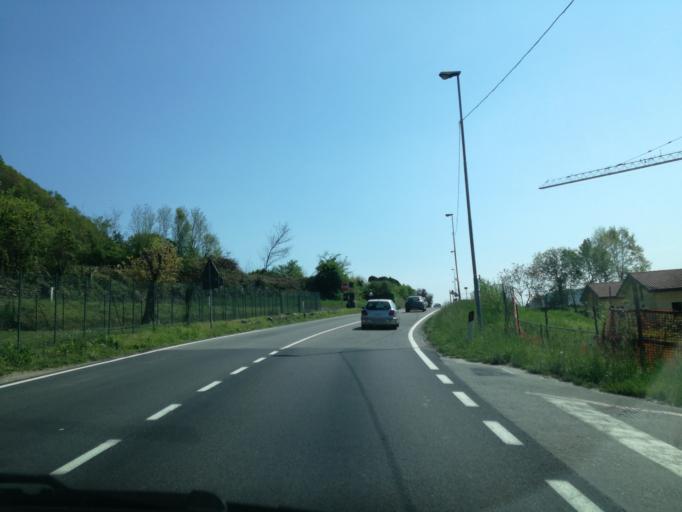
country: IT
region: Lombardy
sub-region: Provincia di Bergamo
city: Villa d'Adda
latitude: 45.7247
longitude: 9.4560
